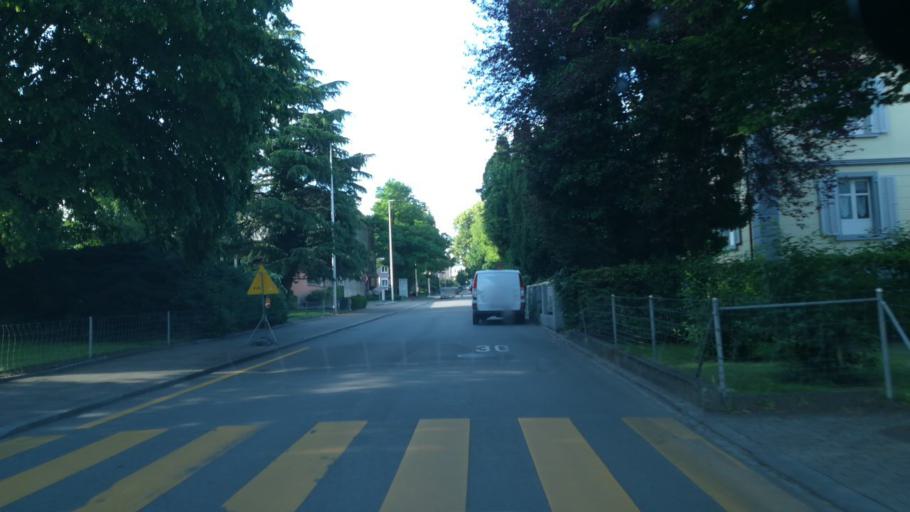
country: DE
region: Baden-Wuerttemberg
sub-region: Freiburg Region
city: Konstanz
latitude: 47.6495
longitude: 9.1693
